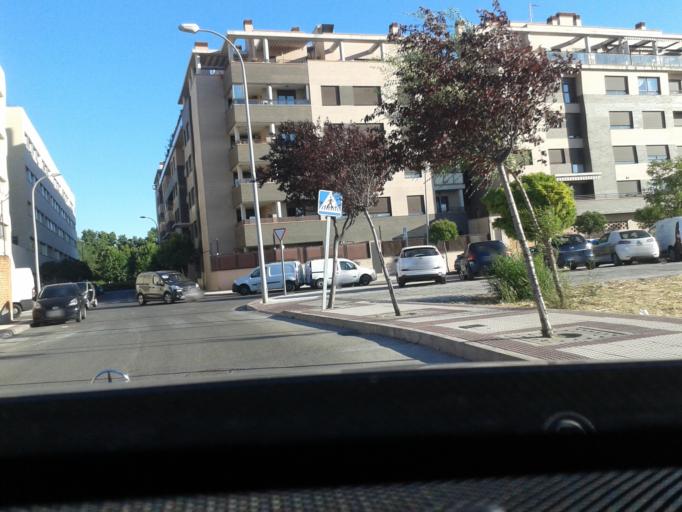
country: ES
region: Madrid
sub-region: Provincia de Madrid
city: Alcala de Henares
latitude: 40.4823
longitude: -3.3770
